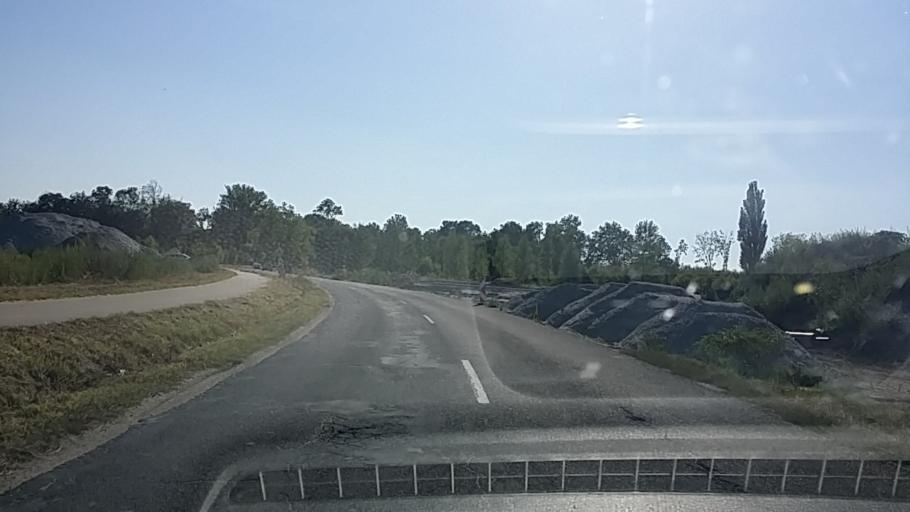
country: HU
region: Gyor-Moson-Sopron
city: Fertod
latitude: 47.6264
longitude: 16.8752
